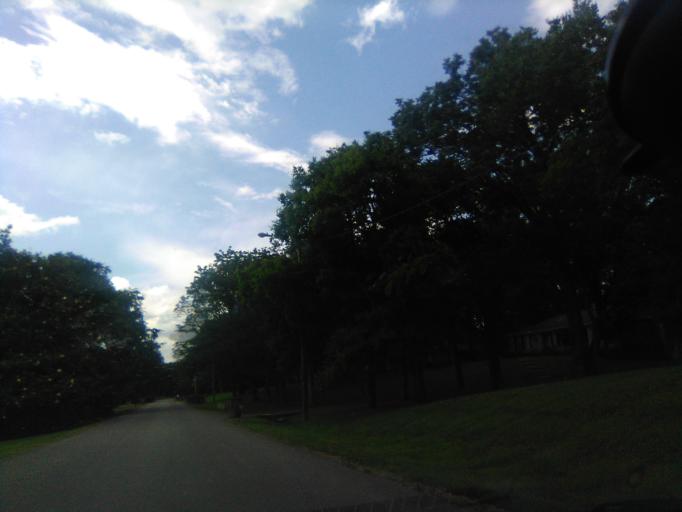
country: US
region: Tennessee
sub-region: Davidson County
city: Belle Meade
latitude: 36.1225
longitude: -86.8770
